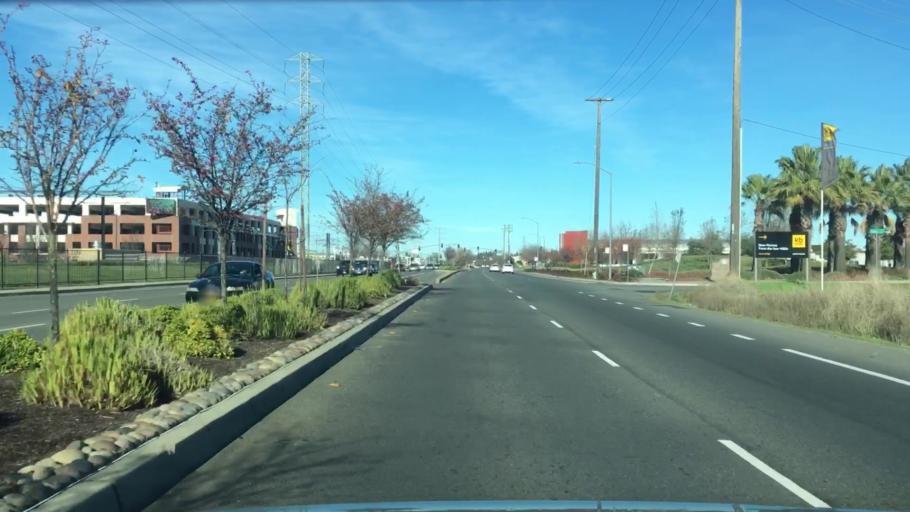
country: US
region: California
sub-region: Sacramento County
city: Laguna
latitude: 38.4501
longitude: -121.4179
